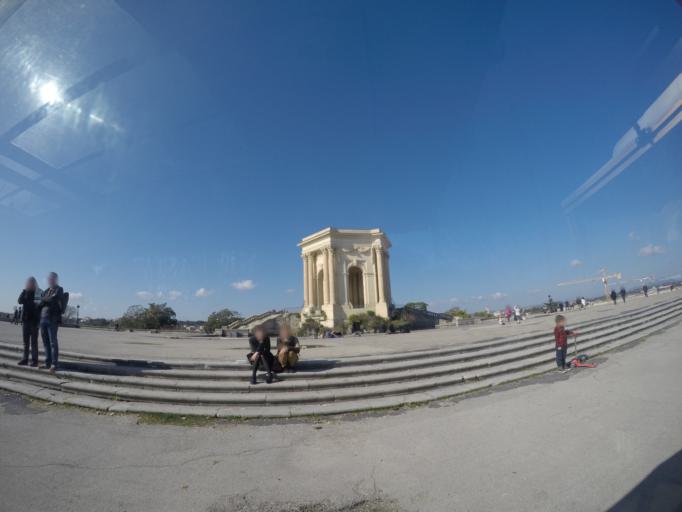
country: FR
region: Languedoc-Roussillon
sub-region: Departement de l'Herault
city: Montpellier
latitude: 43.6112
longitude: 3.8698
